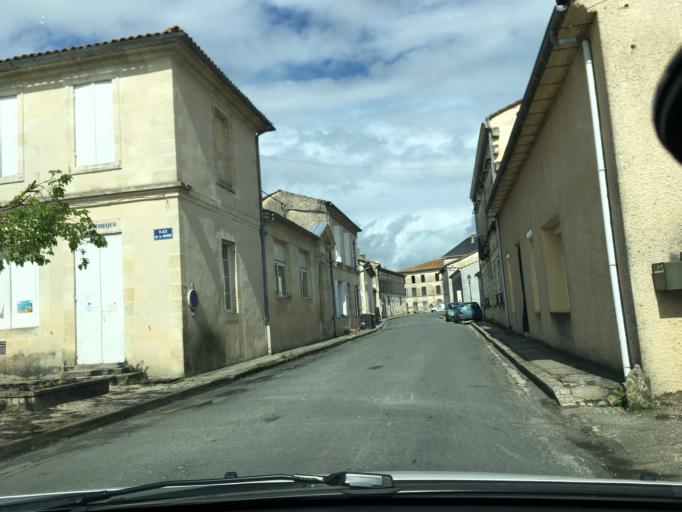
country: FR
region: Aquitaine
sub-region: Departement de la Gironde
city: Vertheuil
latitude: 45.3222
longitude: -0.8204
